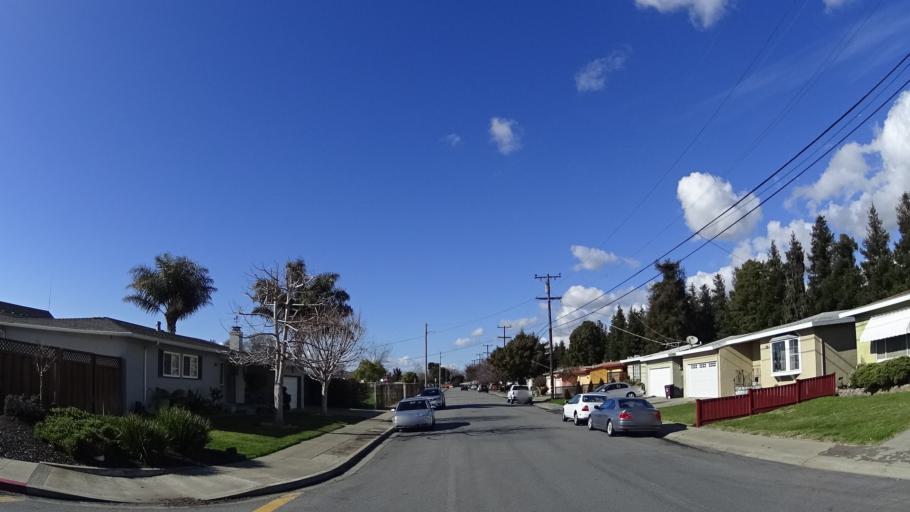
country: US
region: California
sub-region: Alameda County
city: San Lorenzo
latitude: 37.6745
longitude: -122.1159
